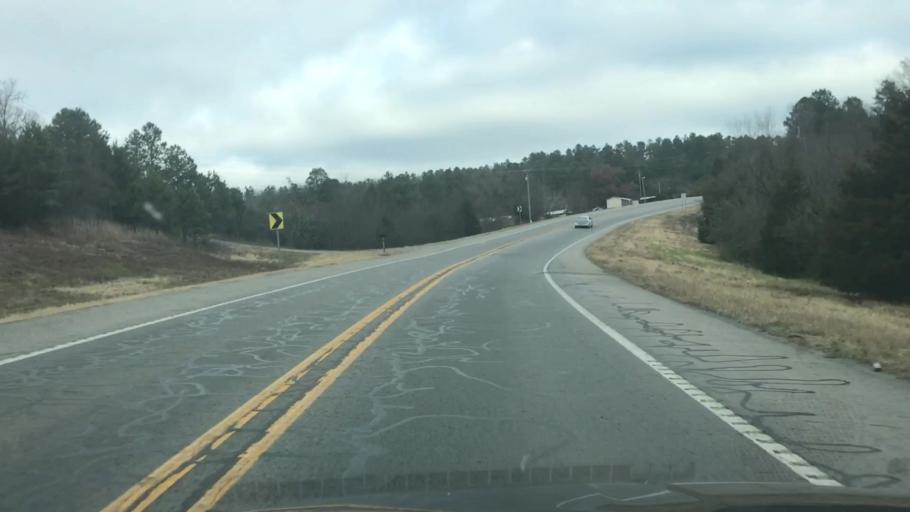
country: US
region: Arkansas
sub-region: Scott County
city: Waldron
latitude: 34.8114
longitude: -94.0404
